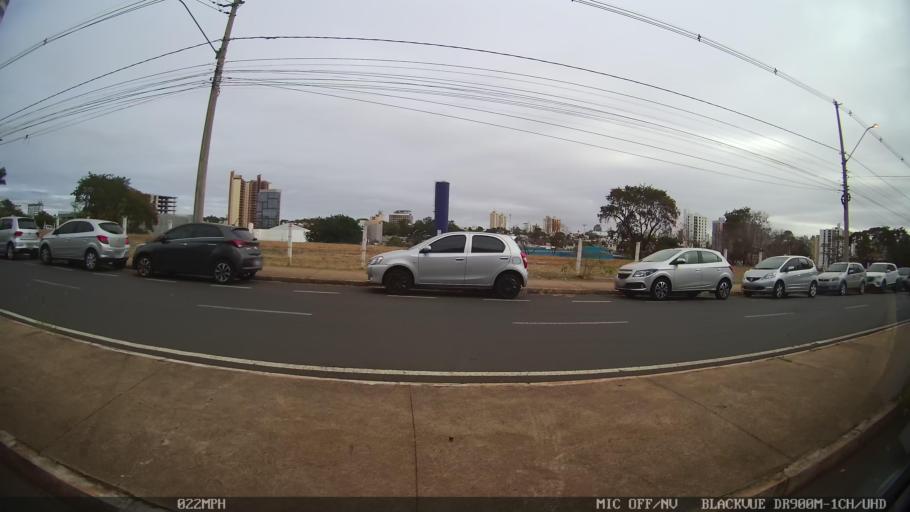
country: BR
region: Sao Paulo
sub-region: Sao Jose Do Rio Preto
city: Sao Jose do Rio Preto
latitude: -20.8259
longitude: -49.3832
